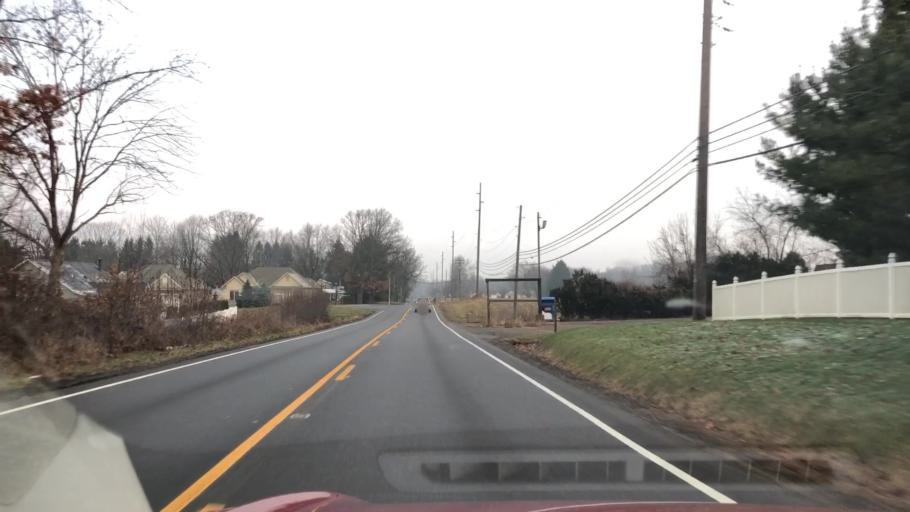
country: US
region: Ohio
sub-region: Stark County
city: Massillon
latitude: 40.8450
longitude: -81.5213
